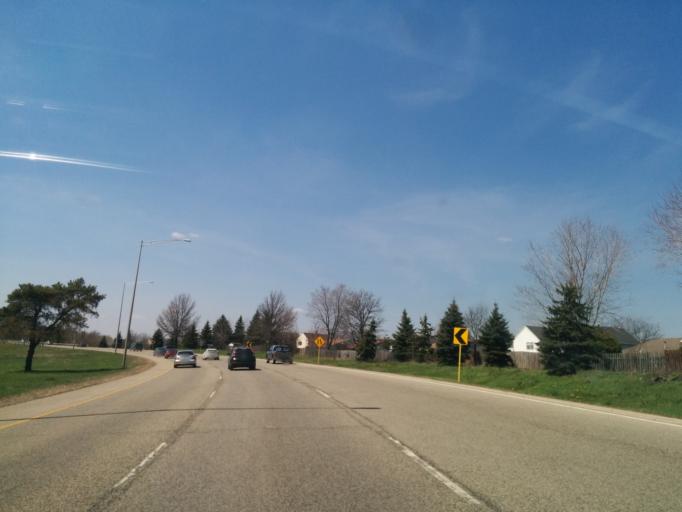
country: US
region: Illinois
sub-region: Kane County
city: Elgin
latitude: 42.0212
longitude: -88.2420
